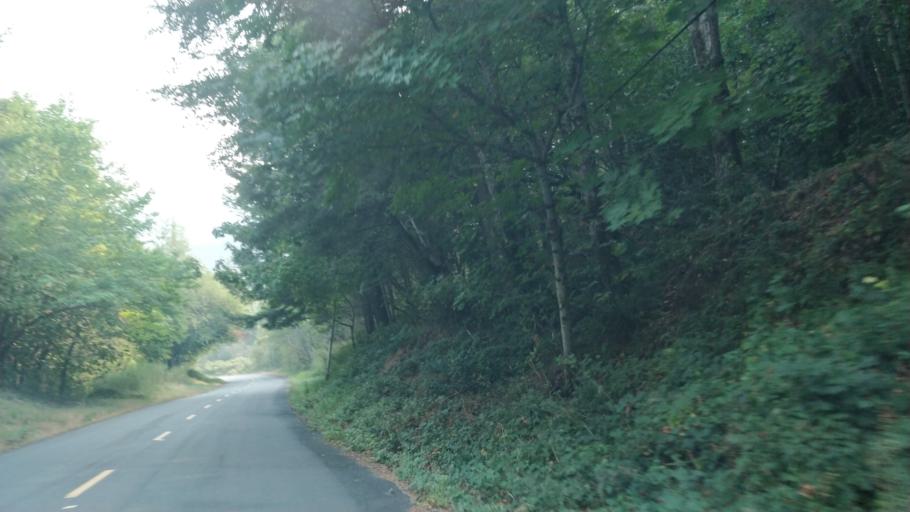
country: US
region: California
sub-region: Humboldt County
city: Rio Dell
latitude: 40.2870
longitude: -124.2529
